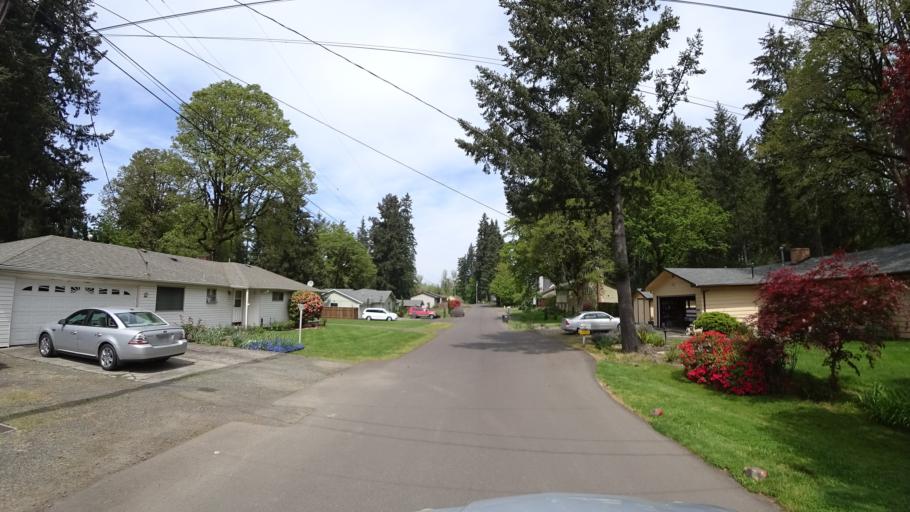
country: US
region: Oregon
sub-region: Washington County
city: Hillsboro
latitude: 45.5041
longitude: -122.9364
